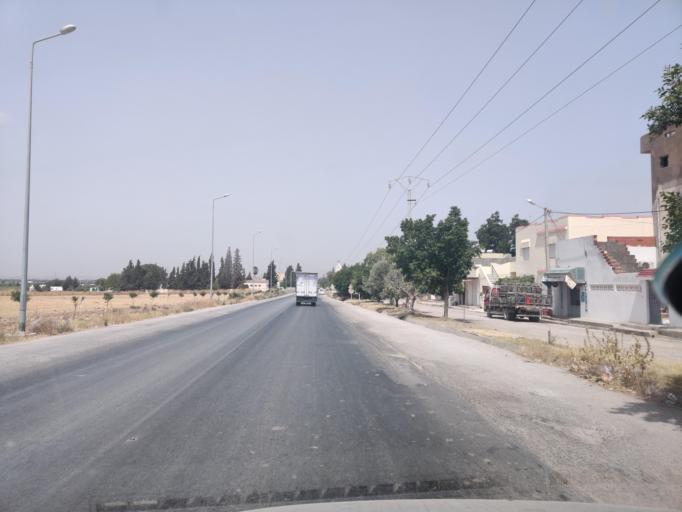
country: TN
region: Tunis
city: La Sebala du Mornag
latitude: 36.6601
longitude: 10.3277
